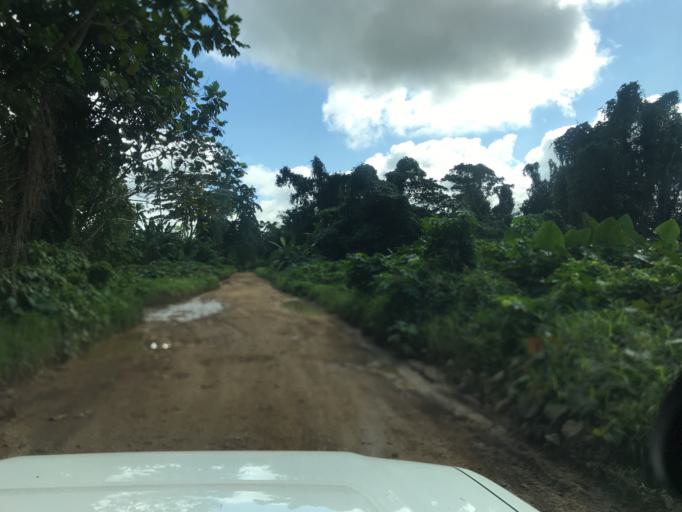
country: VU
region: Sanma
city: Luganville
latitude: -15.4935
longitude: 167.0895
